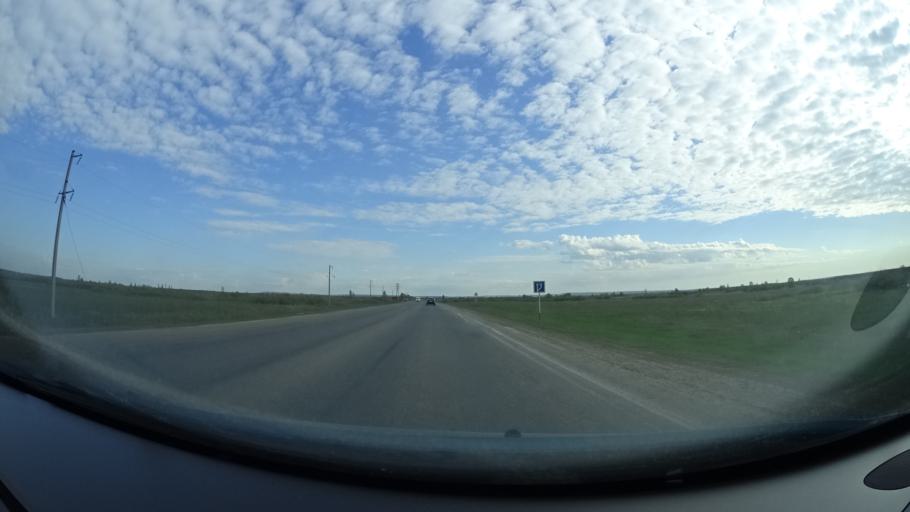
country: RU
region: Bashkortostan
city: Mikhaylovka
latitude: 54.9748
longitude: 55.7678
